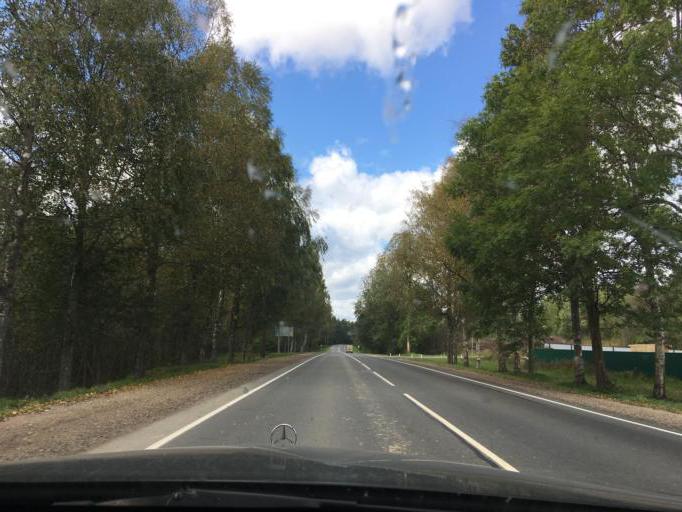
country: RU
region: Pskov
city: Pustoshka
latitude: 56.4026
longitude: 29.2247
